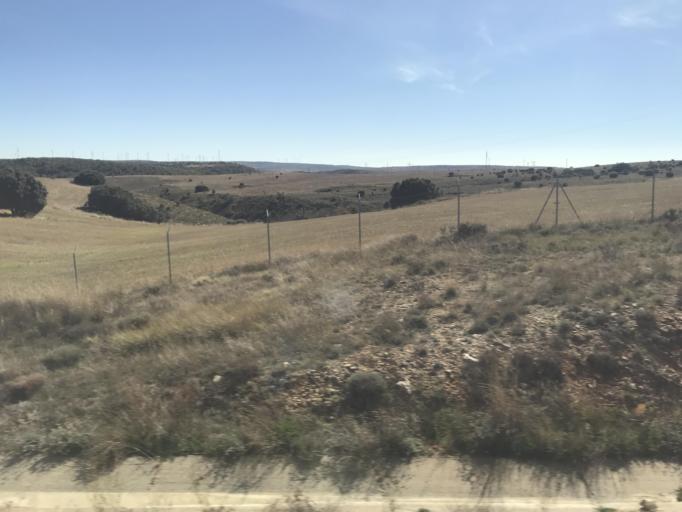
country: ES
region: Castille-La Mancha
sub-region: Provincia de Guadalajara
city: Anguita
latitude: 41.1262
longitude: -2.3416
